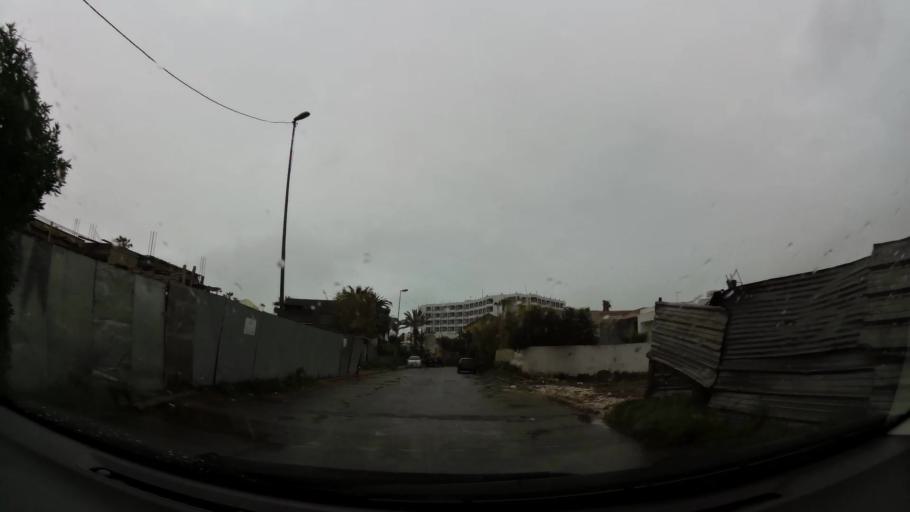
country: MA
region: Grand Casablanca
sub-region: Casablanca
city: Casablanca
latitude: 33.5899
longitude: -7.6755
